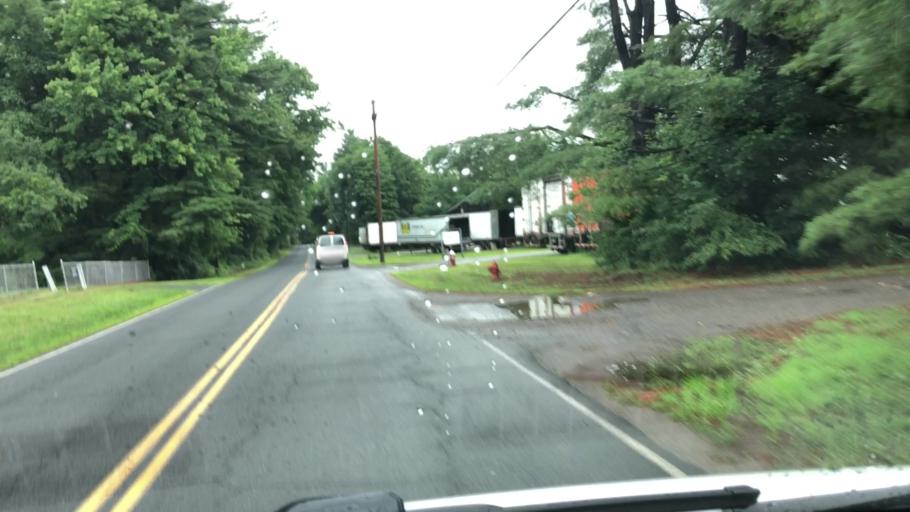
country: US
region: Massachusetts
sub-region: Franklin County
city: South Deerfield
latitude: 42.4638
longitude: -72.6093
